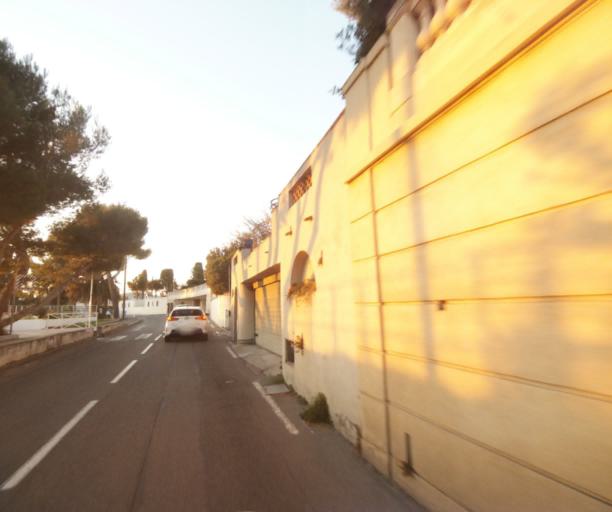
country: FR
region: Provence-Alpes-Cote d'Azur
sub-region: Departement des Alpes-Maritimes
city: Antibes
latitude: 43.5612
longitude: 7.1195
